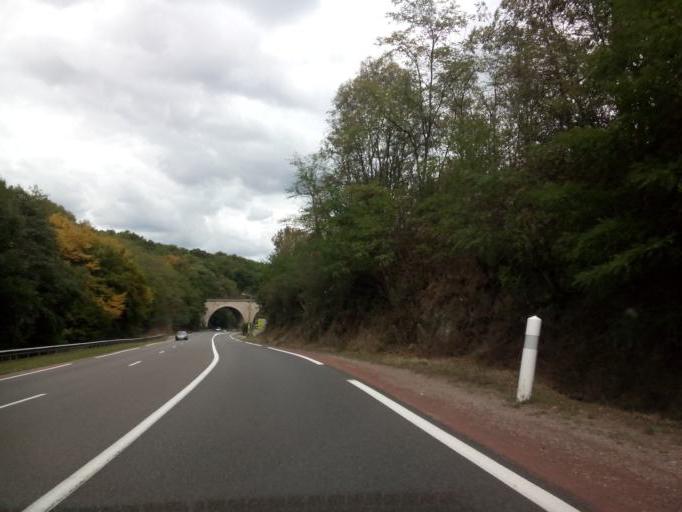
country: FR
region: Rhone-Alpes
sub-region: Departement du Rhone
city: Lissieu
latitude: 45.8496
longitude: 4.7182
